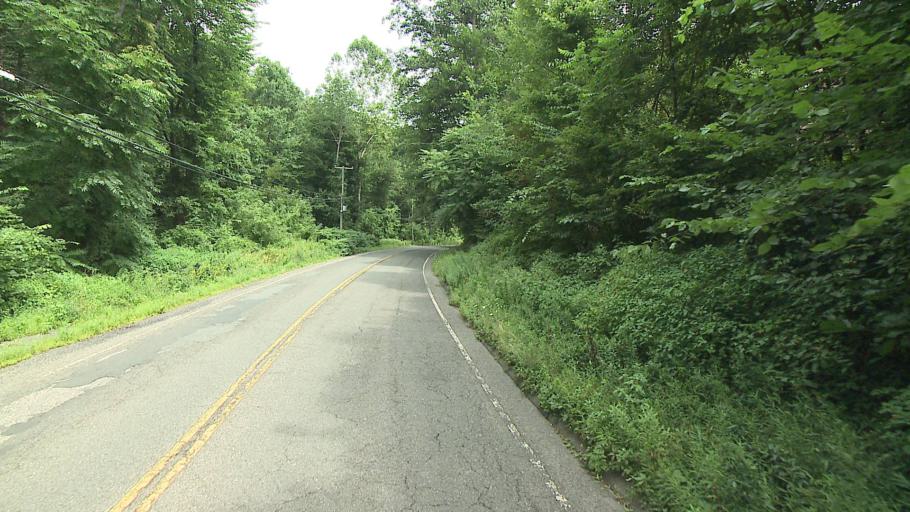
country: US
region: Connecticut
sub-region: Fairfield County
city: Sherman
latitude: 41.6419
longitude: -73.4961
